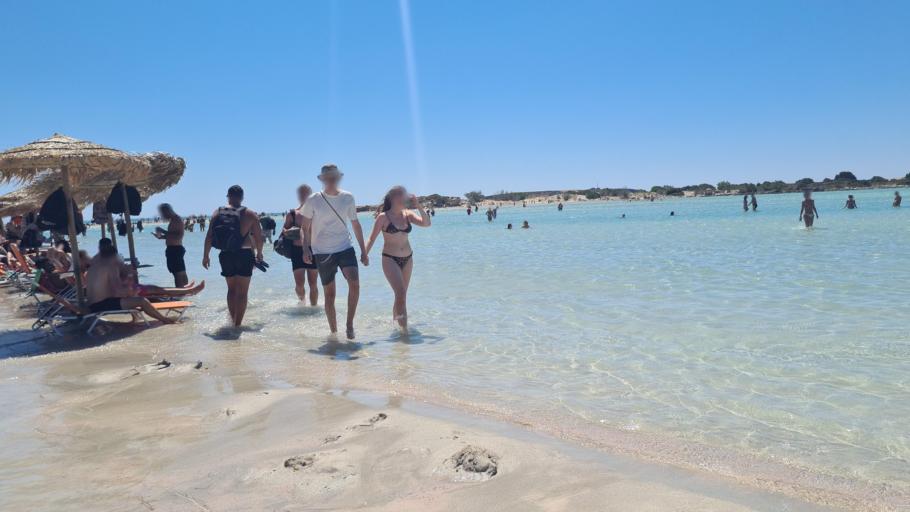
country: GR
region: Crete
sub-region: Nomos Chanias
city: Palaiochora
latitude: 35.2711
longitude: 23.5411
